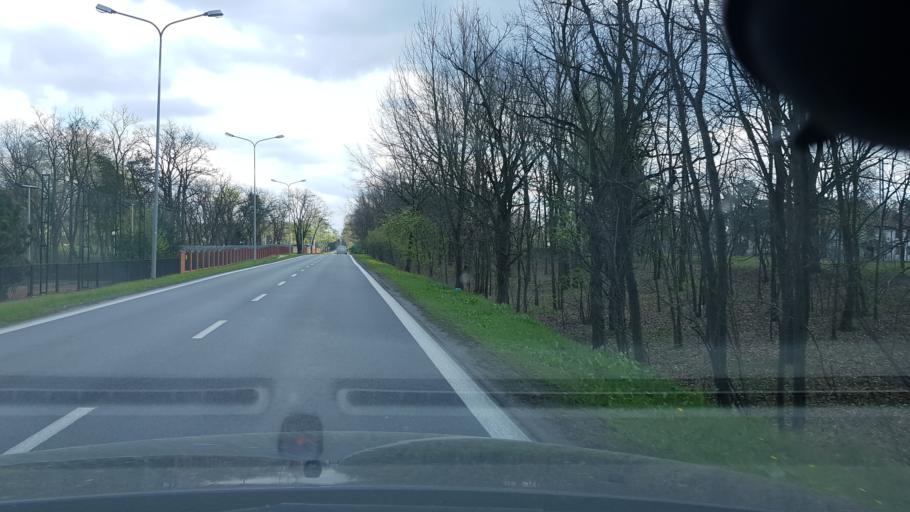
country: PL
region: Masovian Voivodeship
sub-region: Warszawa
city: Wesola
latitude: 52.2542
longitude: 21.2298
